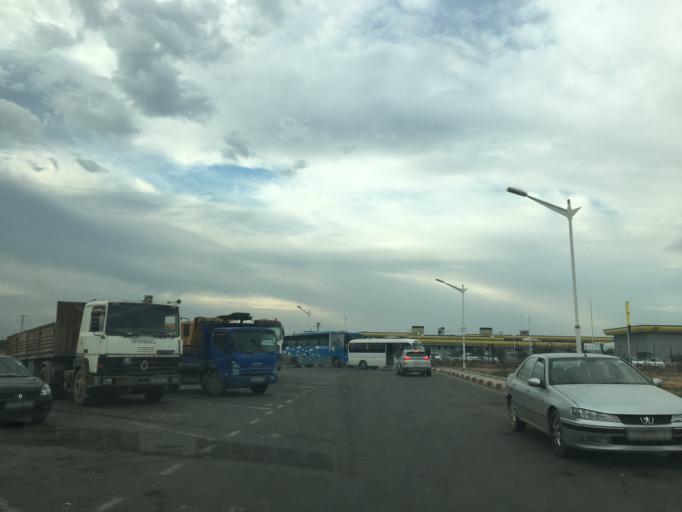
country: DZ
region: Bouira
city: Bouira
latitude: 36.3098
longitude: 4.0622
